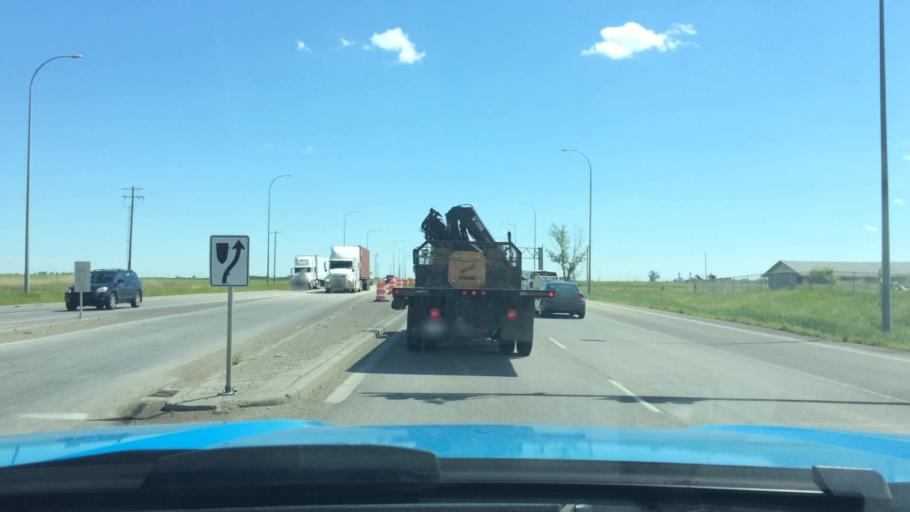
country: CA
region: Alberta
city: Chestermere
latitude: 50.9796
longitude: -113.9351
